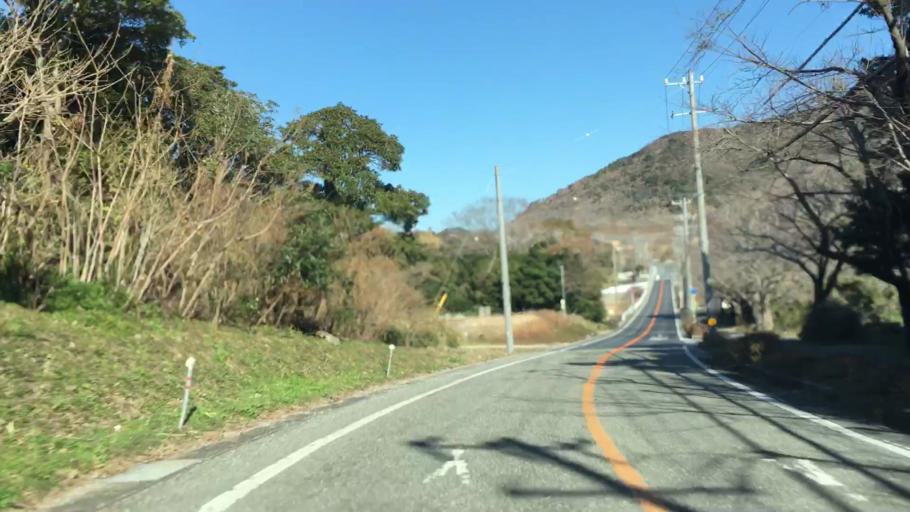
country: JP
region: Aichi
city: Tahara
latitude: 34.6767
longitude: 137.2489
